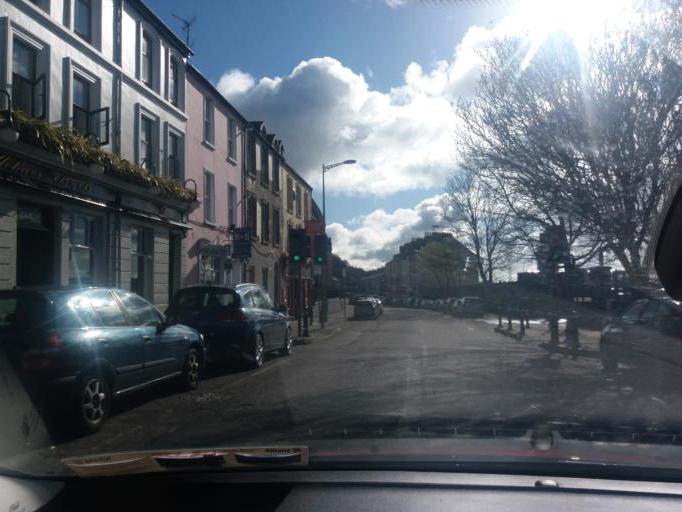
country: IE
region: Munster
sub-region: County Cork
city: Cork
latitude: 51.9024
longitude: -8.4582
